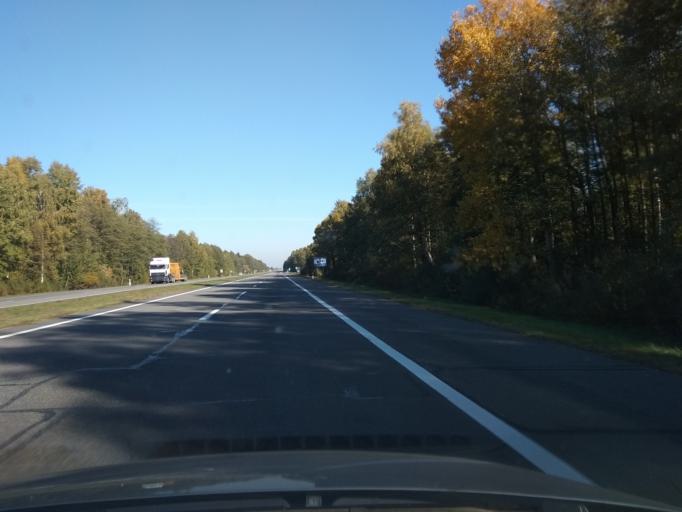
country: BY
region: Brest
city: Ivatsevichy
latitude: 52.6830
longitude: 25.3327
